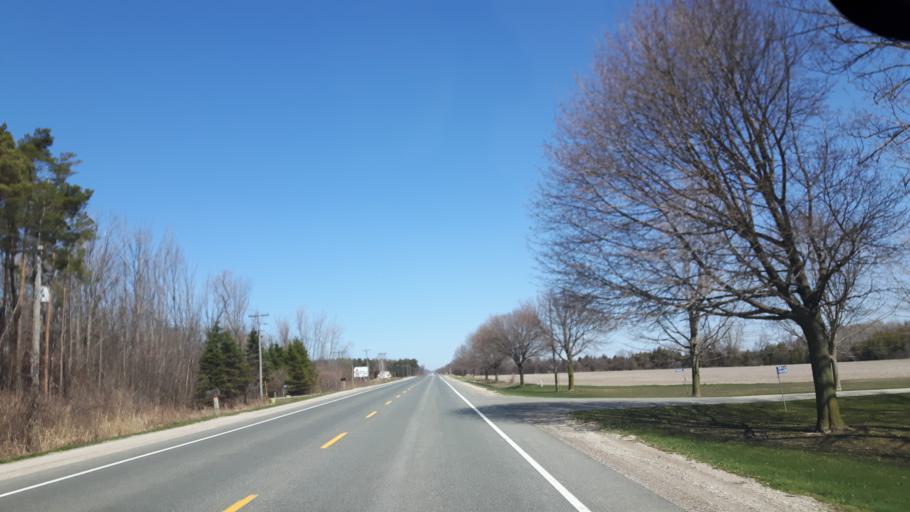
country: CA
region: Ontario
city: Goderich
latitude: 43.7003
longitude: -81.7056
